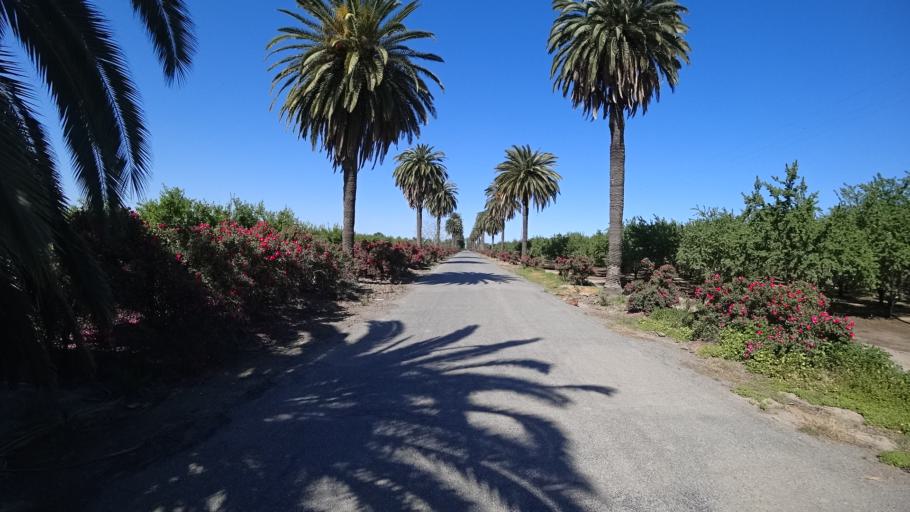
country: US
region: California
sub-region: Glenn County
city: Hamilton City
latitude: 39.7374
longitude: -122.0457
